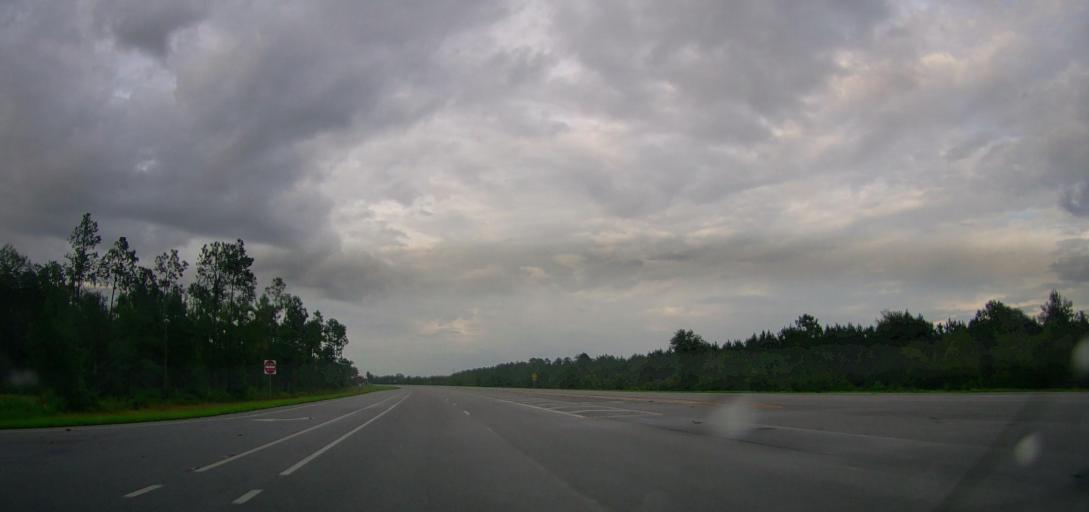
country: US
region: Georgia
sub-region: Ware County
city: Deenwood
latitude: 31.1601
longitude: -82.4228
